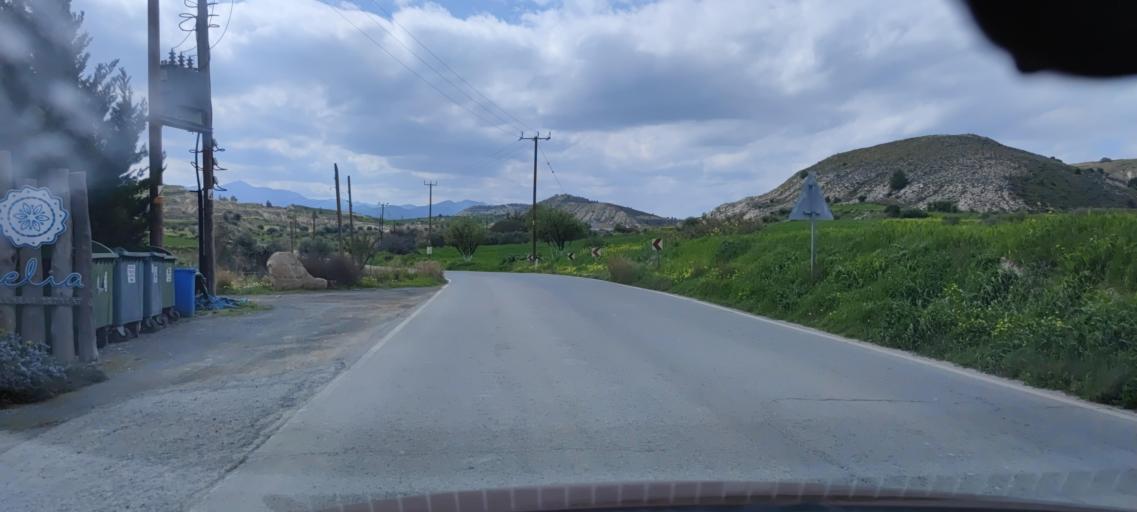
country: CY
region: Lefkosia
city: Tseri
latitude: 35.0273
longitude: 33.3046
